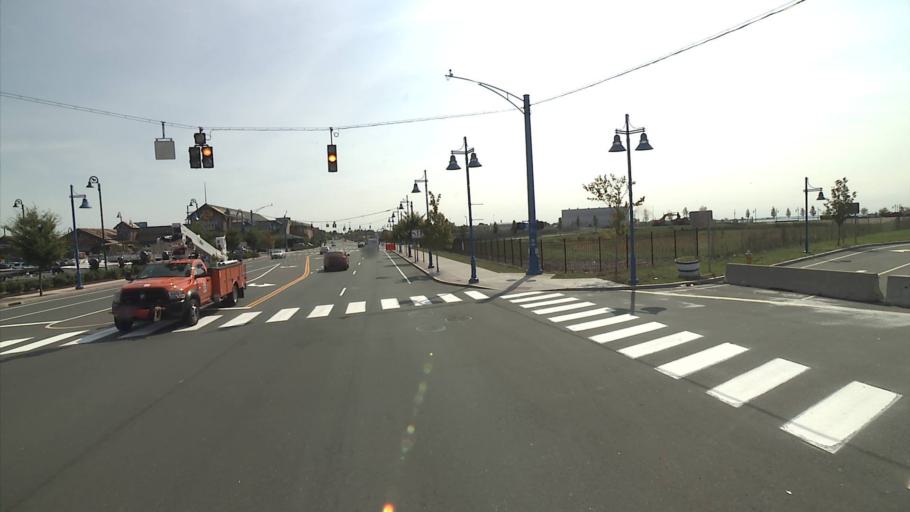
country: US
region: Connecticut
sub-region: Fairfield County
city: Bridgeport
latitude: 41.1777
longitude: -73.1812
